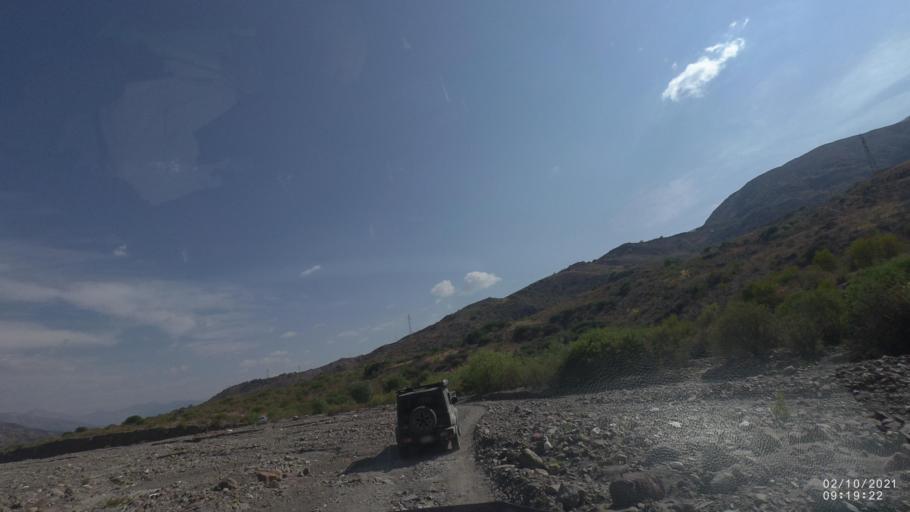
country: BO
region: Cochabamba
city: Irpa Irpa
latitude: -17.8763
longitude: -66.3066
